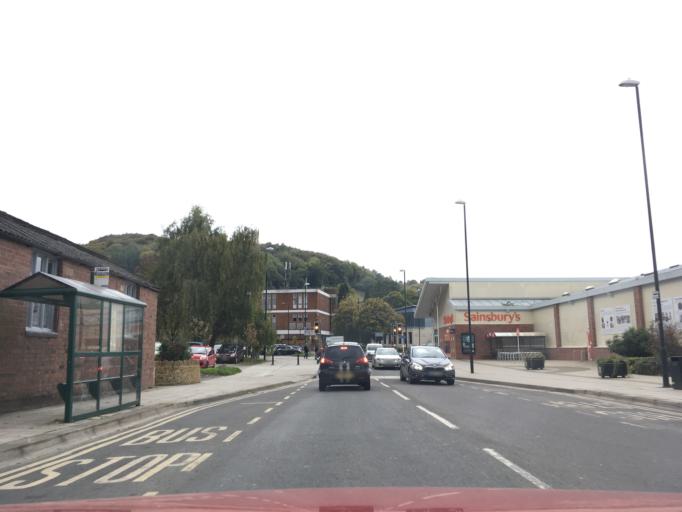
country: GB
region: England
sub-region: Gloucestershire
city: Dursley
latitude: 51.6819
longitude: -2.3547
